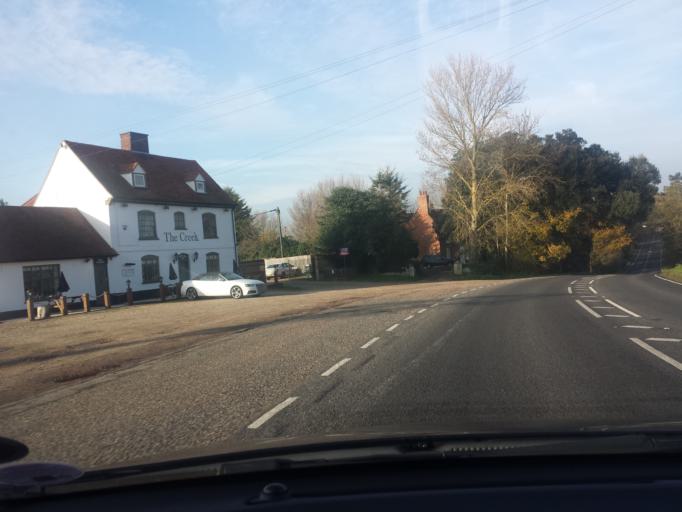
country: GB
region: England
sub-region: Essex
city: Saint Osyth
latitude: 51.8202
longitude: 1.0709
